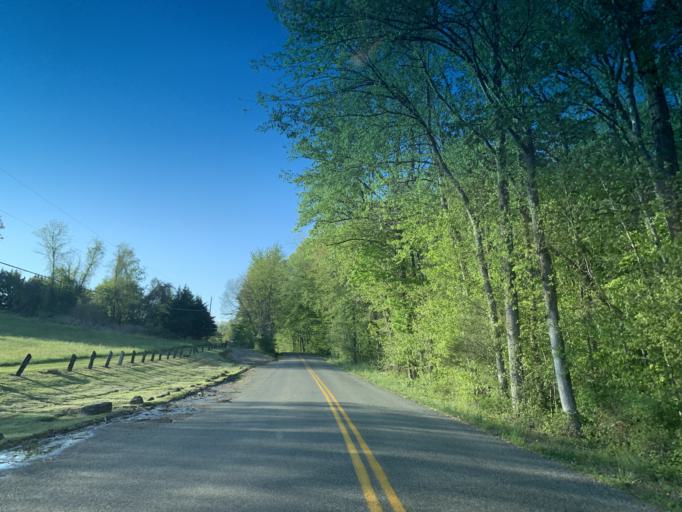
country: US
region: Maryland
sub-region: Harford County
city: Aberdeen
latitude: 39.5446
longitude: -76.1789
